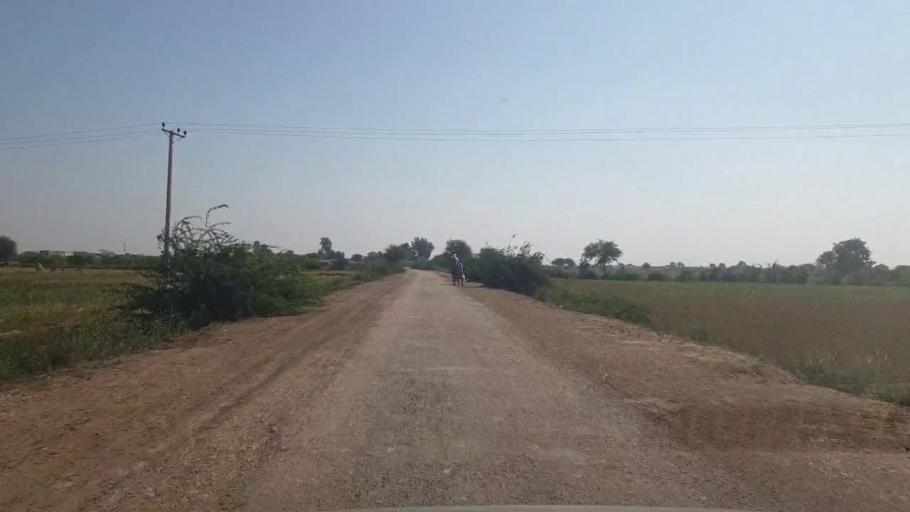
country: PK
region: Sindh
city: Badin
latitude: 24.5738
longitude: 68.8438
